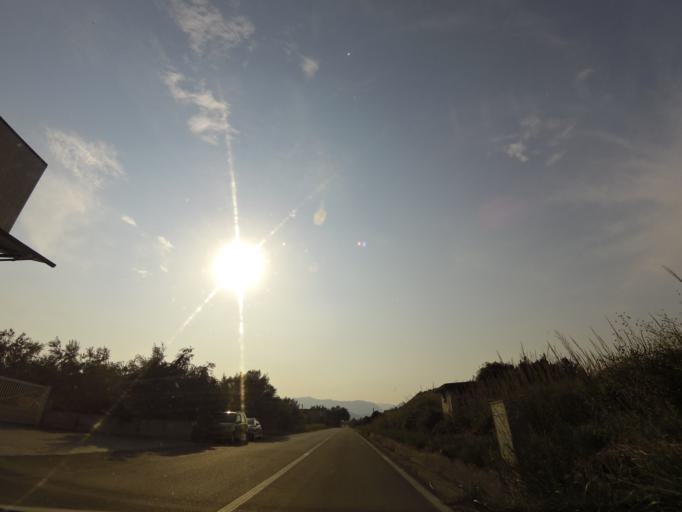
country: IT
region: Calabria
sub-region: Provincia di Reggio Calabria
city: Monasterace
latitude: 38.4378
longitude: 16.5542
